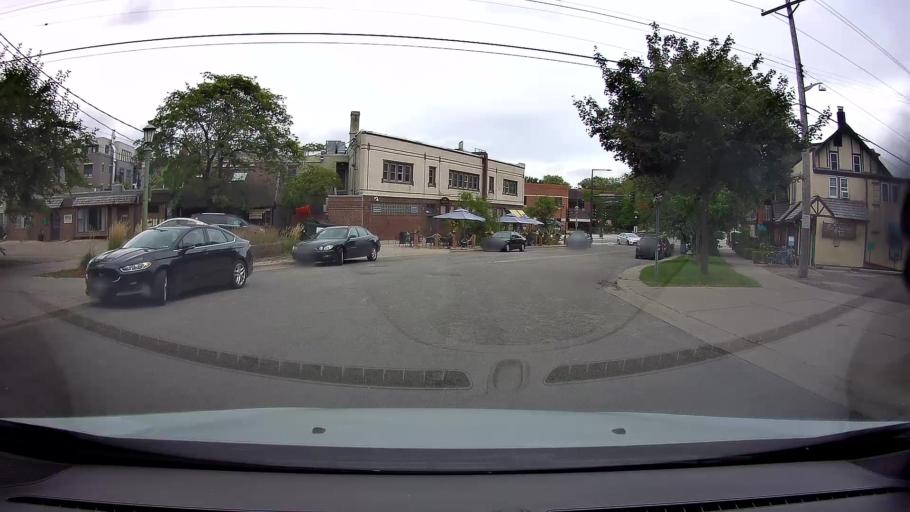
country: US
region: Minnesota
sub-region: Ramsey County
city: Lauderdale
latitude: 44.9813
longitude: -93.1958
